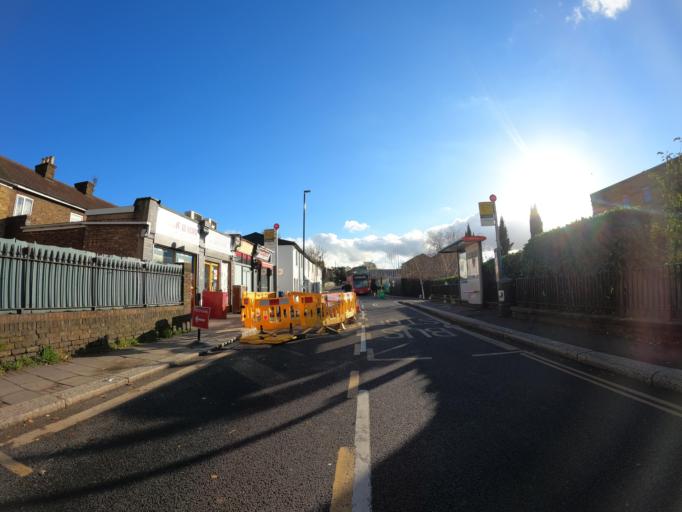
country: GB
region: England
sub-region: Greater London
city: Brentford
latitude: 51.4891
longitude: -0.3085
